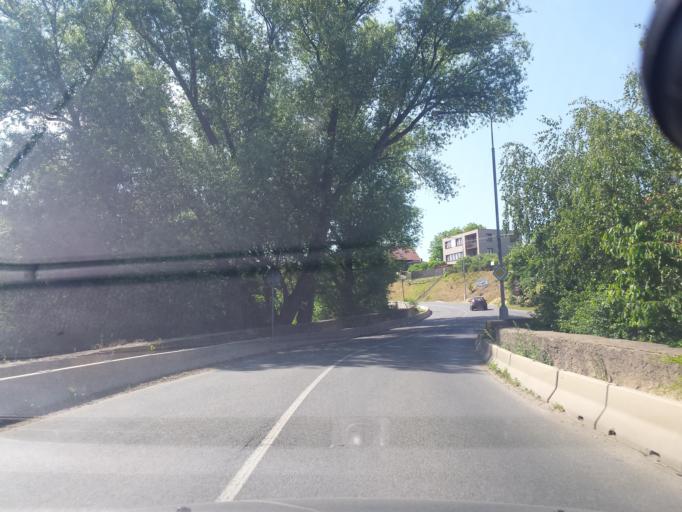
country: CZ
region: Central Bohemia
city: Horomerice
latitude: 50.1482
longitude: 14.3336
